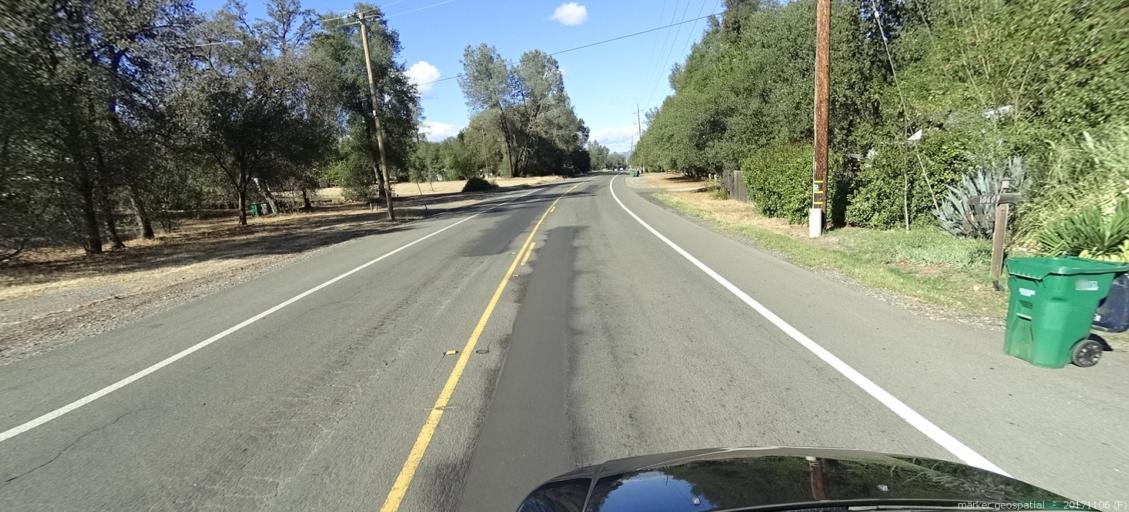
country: US
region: California
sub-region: Shasta County
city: Palo Cedro
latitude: 40.5957
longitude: -122.3108
